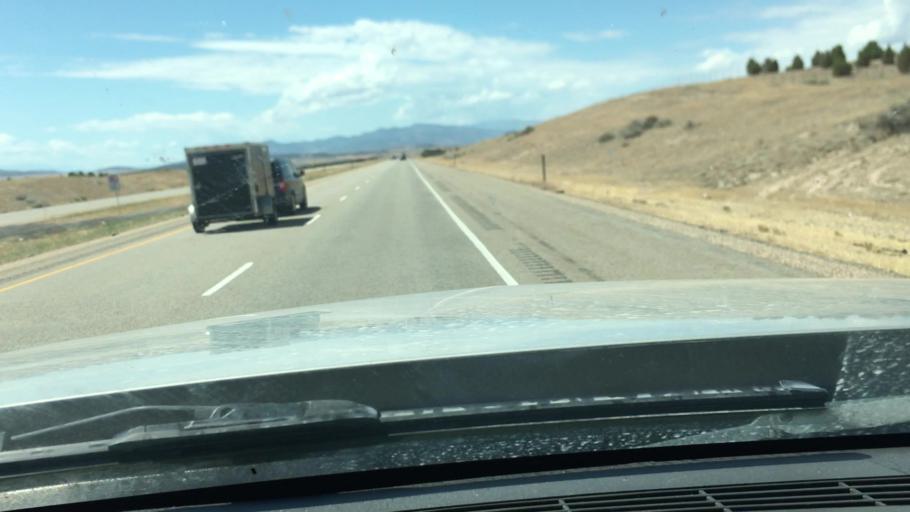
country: US
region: Utah
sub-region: Juab County
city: Nephi
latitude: 39.5432
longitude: -111.9528
